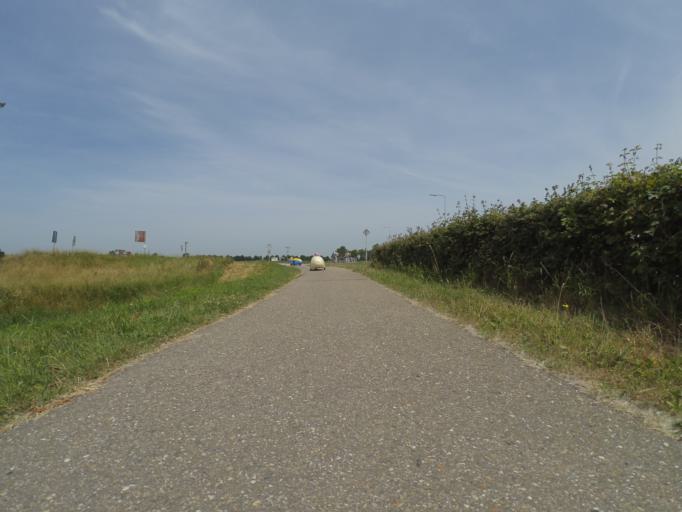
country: NL
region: North Brabant
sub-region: Gemeente Steenbergen
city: Welberg
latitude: 51.6065
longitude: 4.3471
